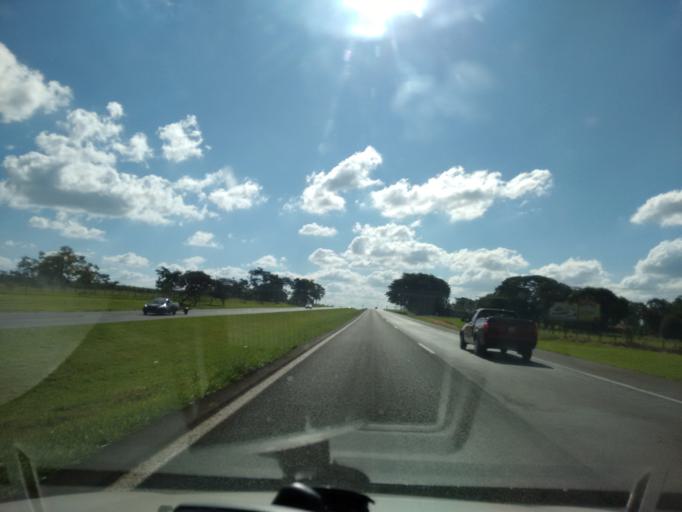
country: BR
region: Sao Paulo
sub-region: Ibate
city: Ibate
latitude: -21.9239
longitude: -48.0297
